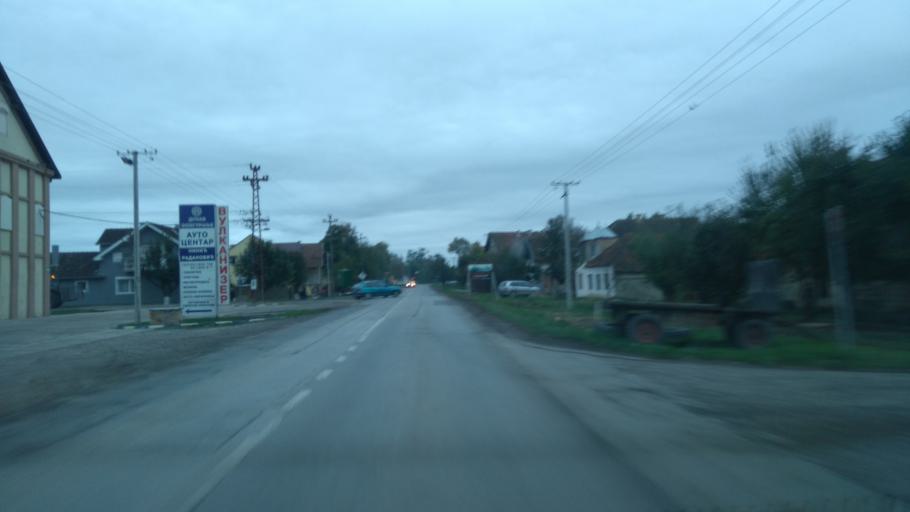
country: RS
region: Autonomna Pokrajina Vojvodina
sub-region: Juznobacki Okrug
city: Zabalj
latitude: 45.3618
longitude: 20.0654
